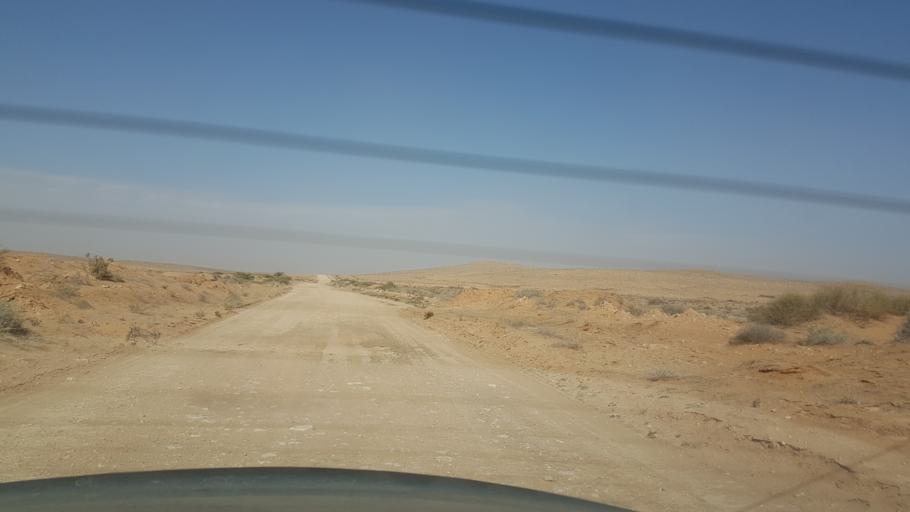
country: TN
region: Qabis
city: El Hamma
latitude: 33.6512
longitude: 9.7365
